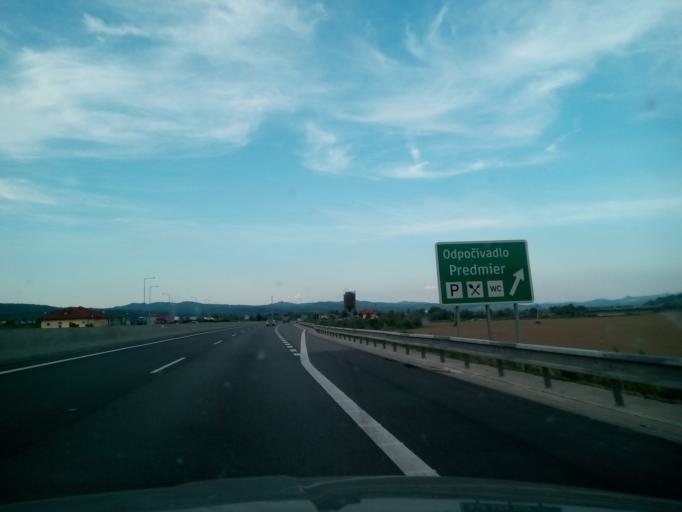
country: SK
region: Zilinsky
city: Bytca
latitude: 49.2004
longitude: 18.5201
